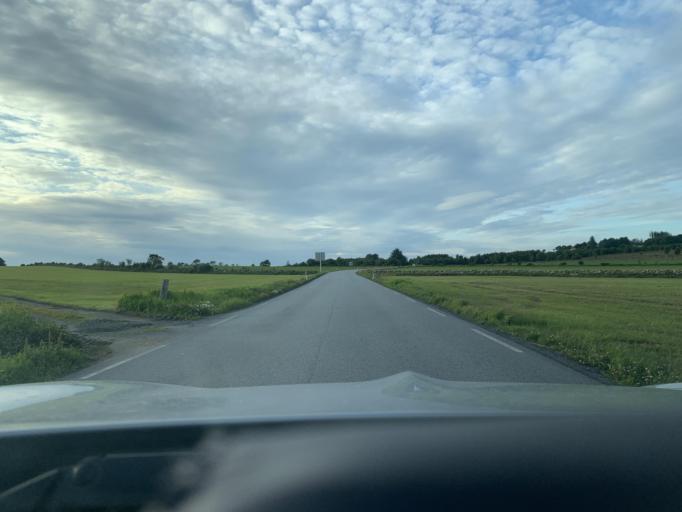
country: NO
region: Rogaland
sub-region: Time
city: Bryne
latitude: 58.6939
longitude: 5.7104
